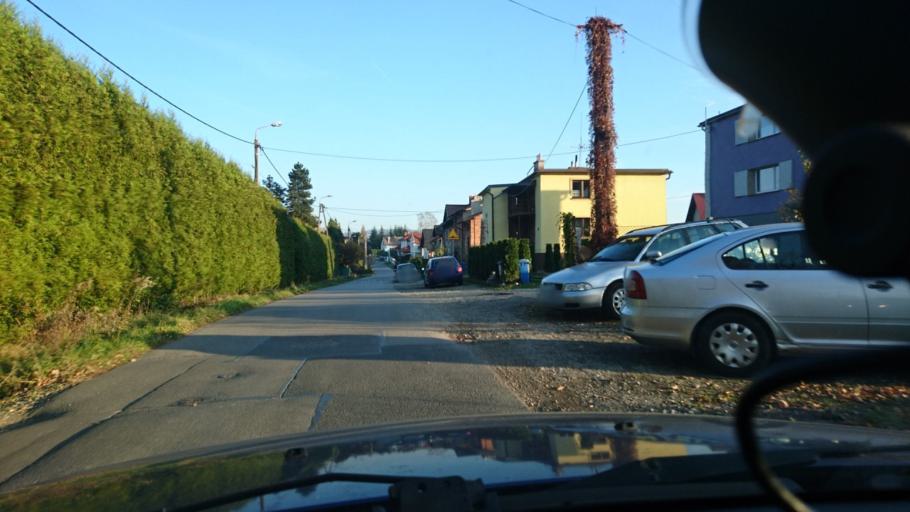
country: PL
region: Silesian Voivodeship
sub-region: Bielsko-Biala
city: Bielsko-Biala
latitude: 49.8617
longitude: 19.0267
